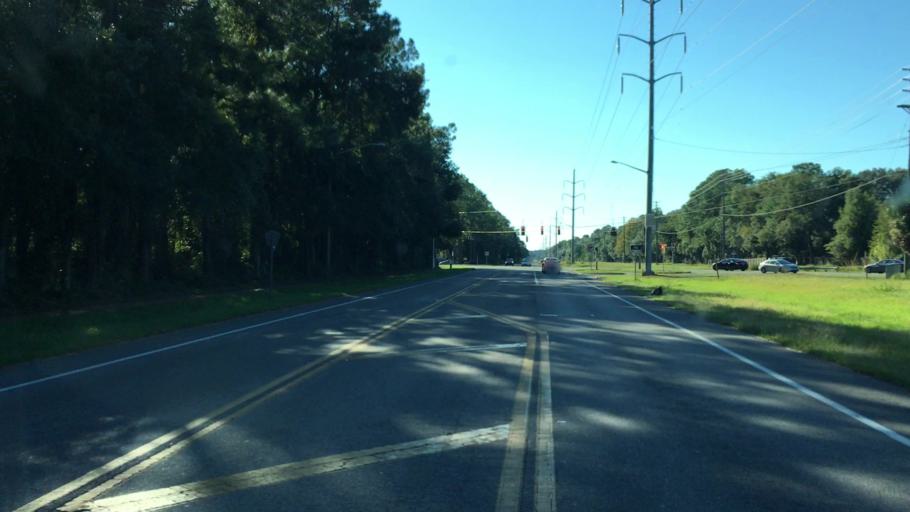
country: US
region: Florida
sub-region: Alachua County
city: Gainesville
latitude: 29.7033
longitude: -82.3622
